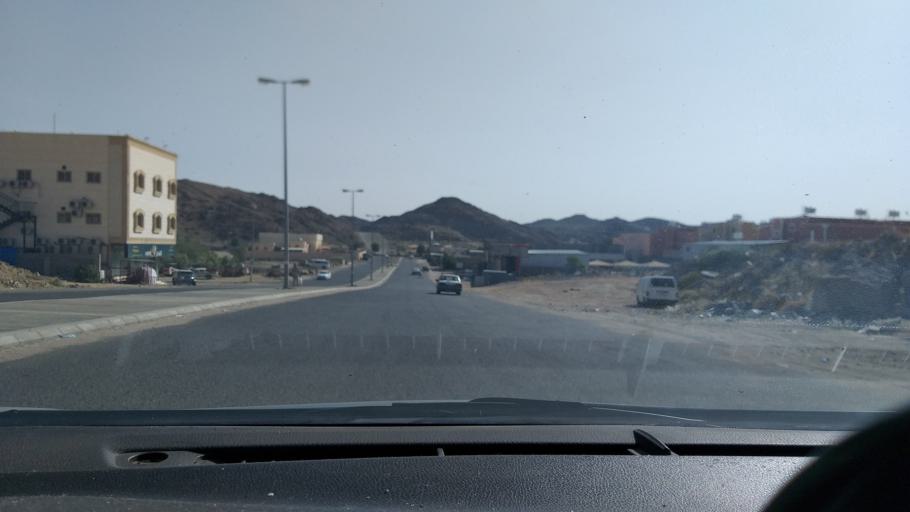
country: SA
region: Makkah
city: Ta'if
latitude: 21.2271
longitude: 40.3780
